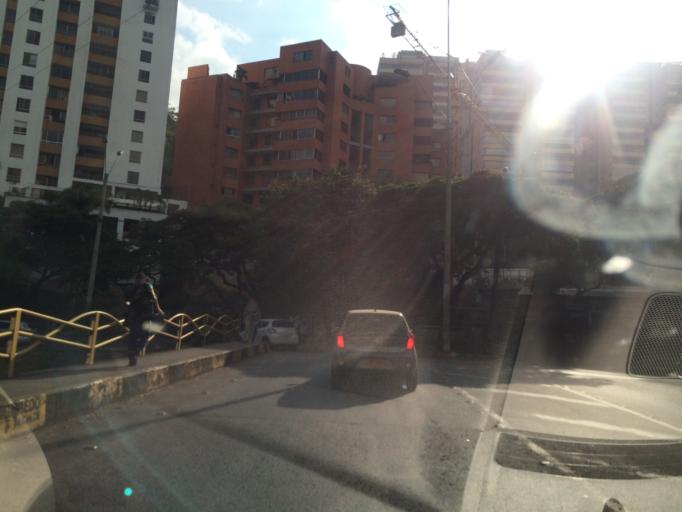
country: CO
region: Valle del Cauca
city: Cali
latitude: 3.4541
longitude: -76.5467
